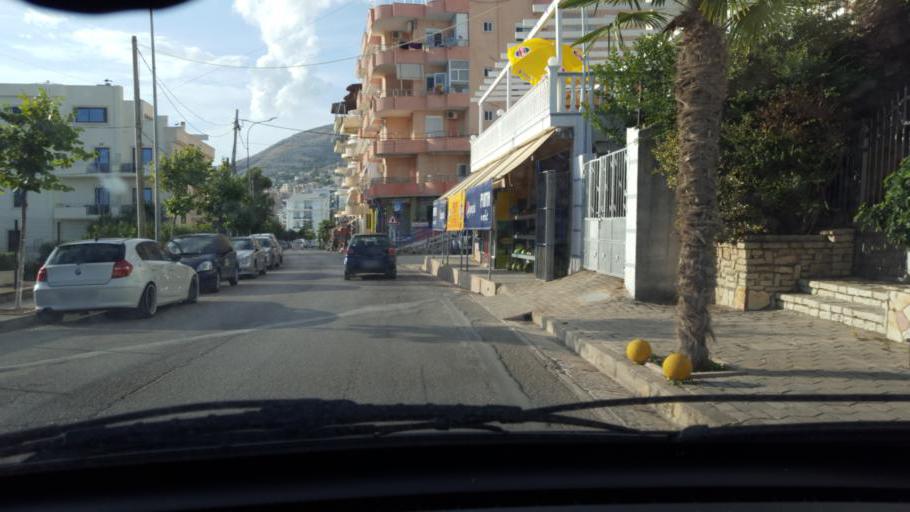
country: AL
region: Vlore
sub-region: Rrethi i Sarandes
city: Sarande
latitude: 39.8678
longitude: 20.0154
